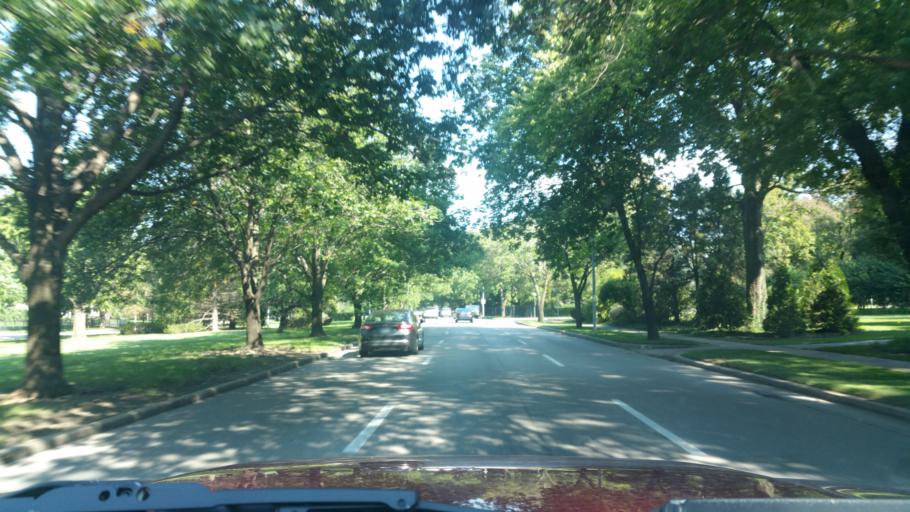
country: US
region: Kansas
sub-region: Johnson County
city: Mission Hills
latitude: 39.0214
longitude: -94.6016
